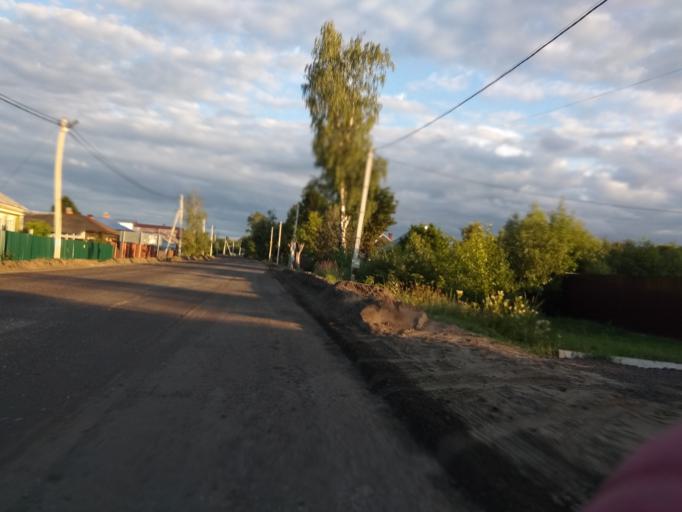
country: RU
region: Moskovskaya
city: Misheronskiy
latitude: 55.6565
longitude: 39.7520
